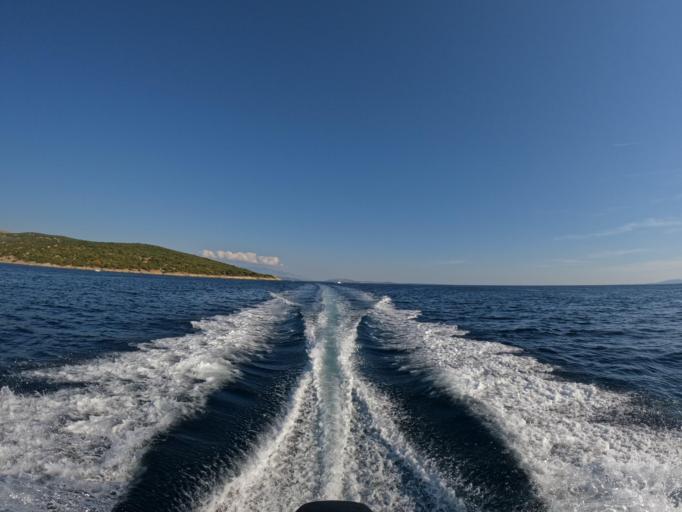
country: HR
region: Primorsko-Goranska
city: Punat
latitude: 44.9855
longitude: 14.6096
